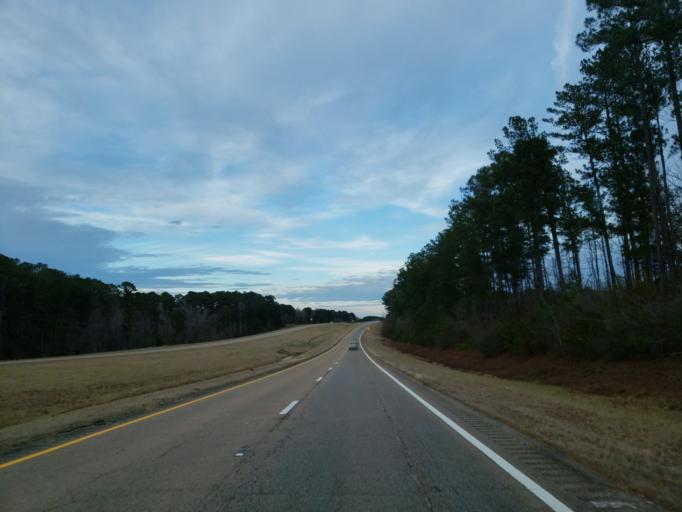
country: US
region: Mississippi
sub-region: Lauderdale County
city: Meridian Station
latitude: 32.4862
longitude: -88.5904
